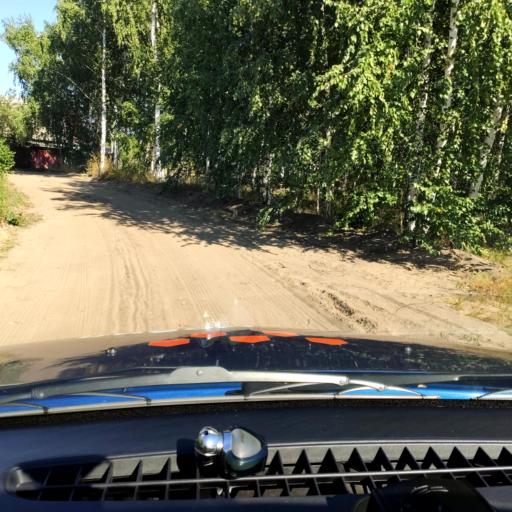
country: RU
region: Voronezj
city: Maslovka
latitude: 51.5436
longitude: 39.1733
